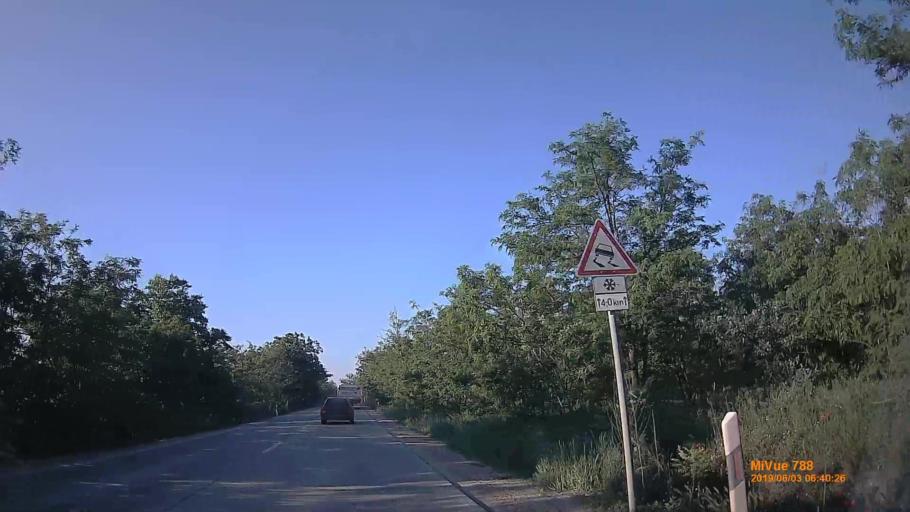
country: HU
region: Pest
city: Dunavarsany
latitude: 47.2787
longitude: 19.1057
